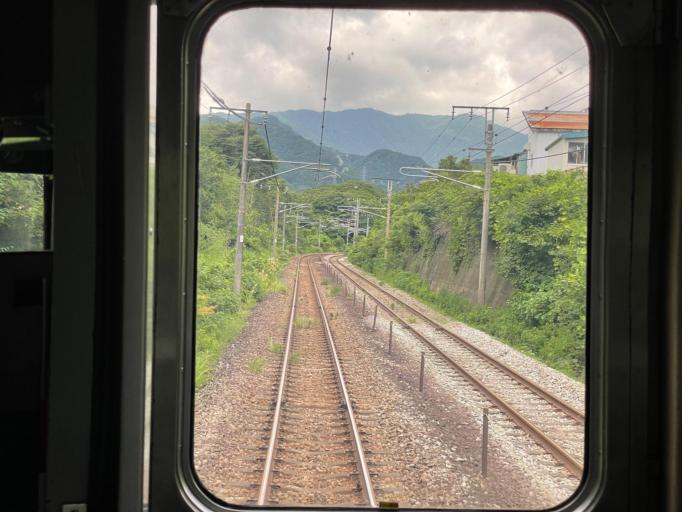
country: JP
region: Gunma
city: Numata
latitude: 36.7468
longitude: 138.9832
